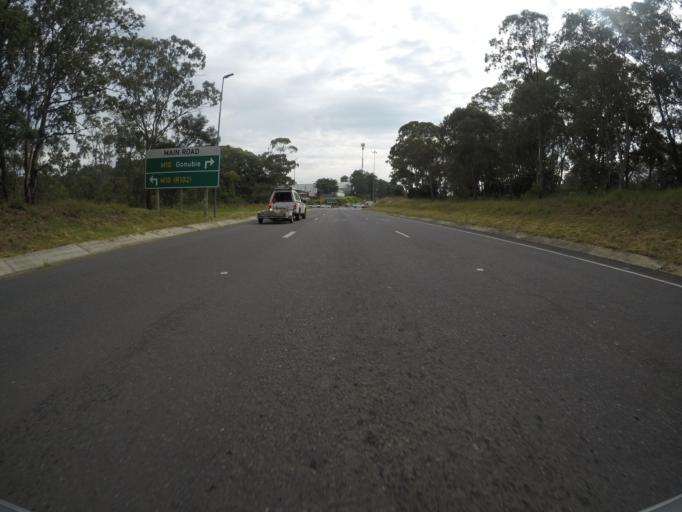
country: ZA
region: Eastern Cape
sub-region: Buffalo City Metropolitan Municipality
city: East London
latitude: -32.9385
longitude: 27.9501
